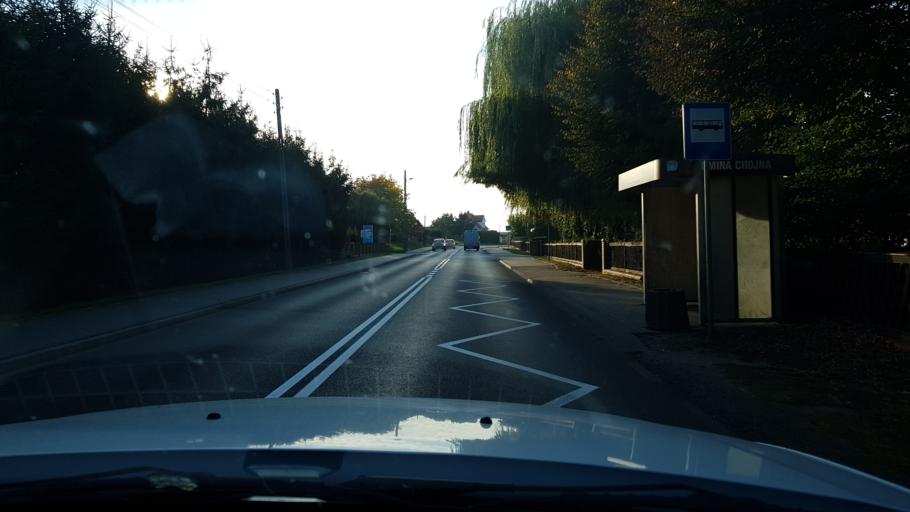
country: PL
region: West Pomeranian Voivodeship
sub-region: Powiat gryfinski
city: Chojna
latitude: 52.9625
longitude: 14.4172
